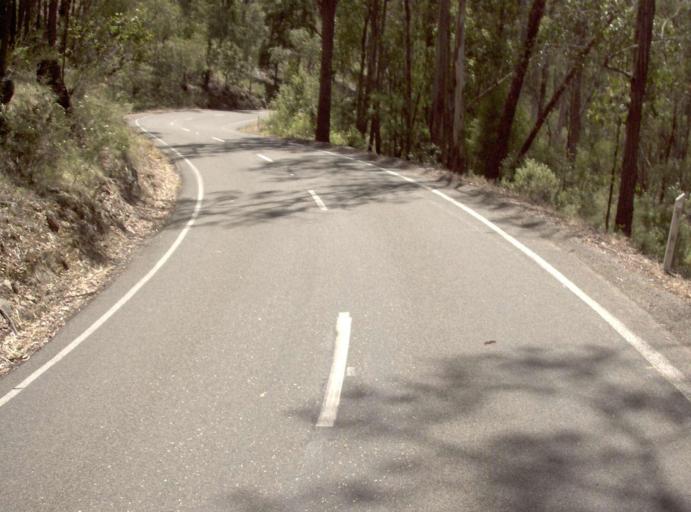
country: AU
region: Victoria
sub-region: East Gippsland
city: Lakes Entrance
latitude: -37.6006
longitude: 147.8884
